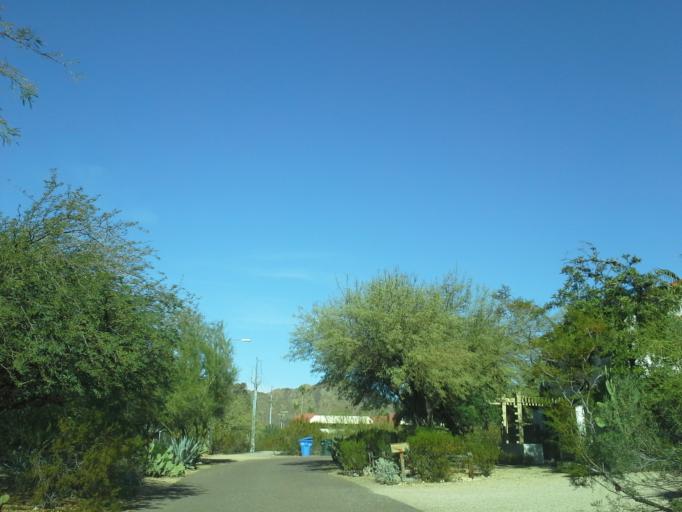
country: US
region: Arizona
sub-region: Maricopa County
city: Paradise Valley
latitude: 33.5528
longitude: -112.0469
